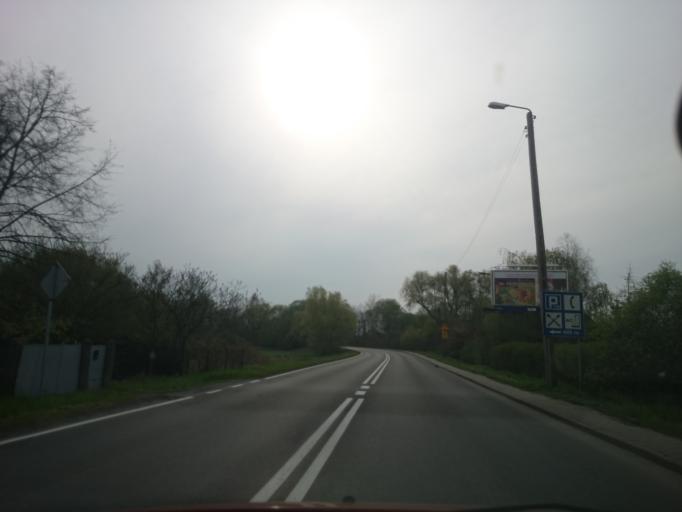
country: PL
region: Opole Voivodeship
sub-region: Powiat opolski
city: Chmielowice
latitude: 50.6819
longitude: 17.8535
